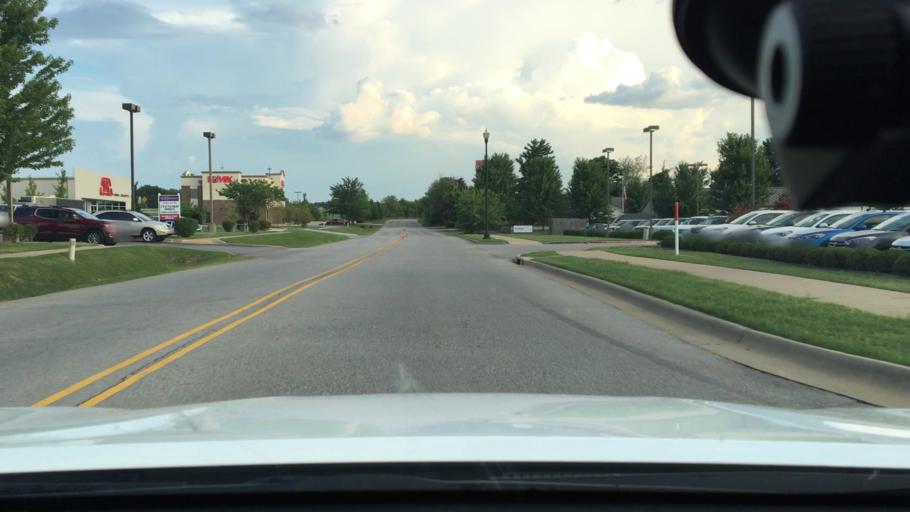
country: US
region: Arkansas
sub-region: Benton County
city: Bentonville
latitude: 36.3394
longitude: -94.1839
